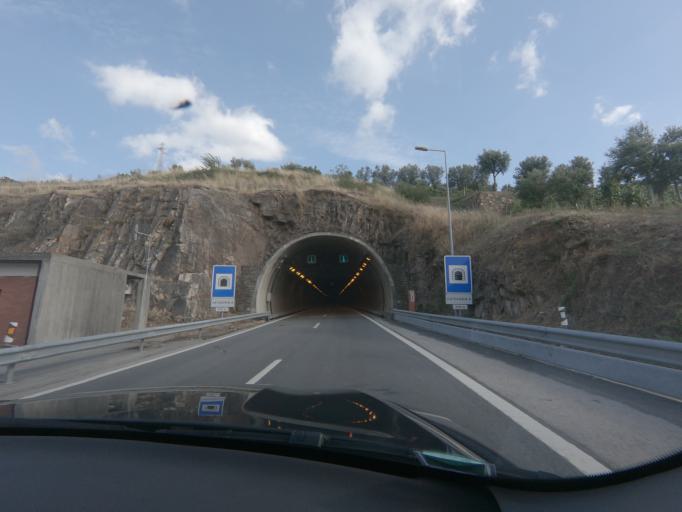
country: PT
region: Viseu
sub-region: Lamego
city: Lamego
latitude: 41.1233
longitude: -7.7797
